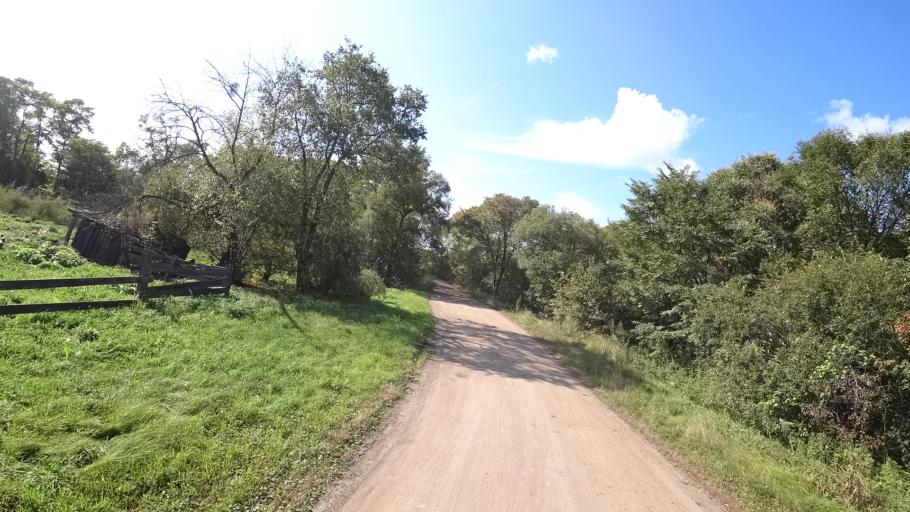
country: RU
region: Amur
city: Arkhara
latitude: 49.4020
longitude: 130.1524
